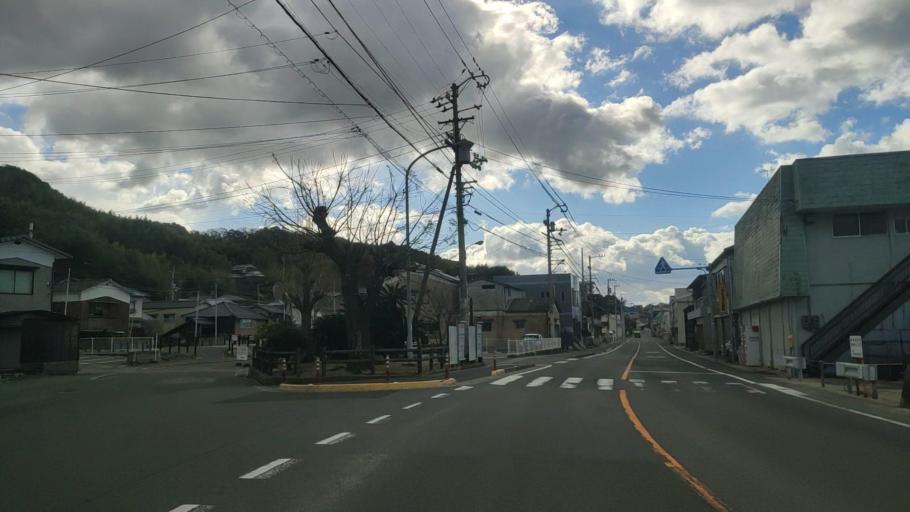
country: JP
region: Ehime
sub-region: Shikoku-chuo Shi
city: Matsuyama
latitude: 33.8847
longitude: 132.7015
